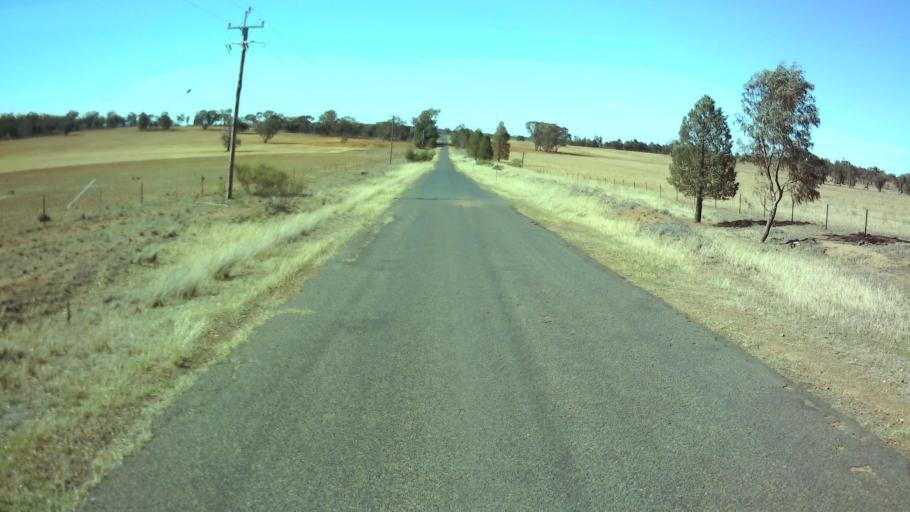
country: AU
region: New South Wales
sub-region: Weddin
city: Grenfell
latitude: -33.7623
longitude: 147.8292
